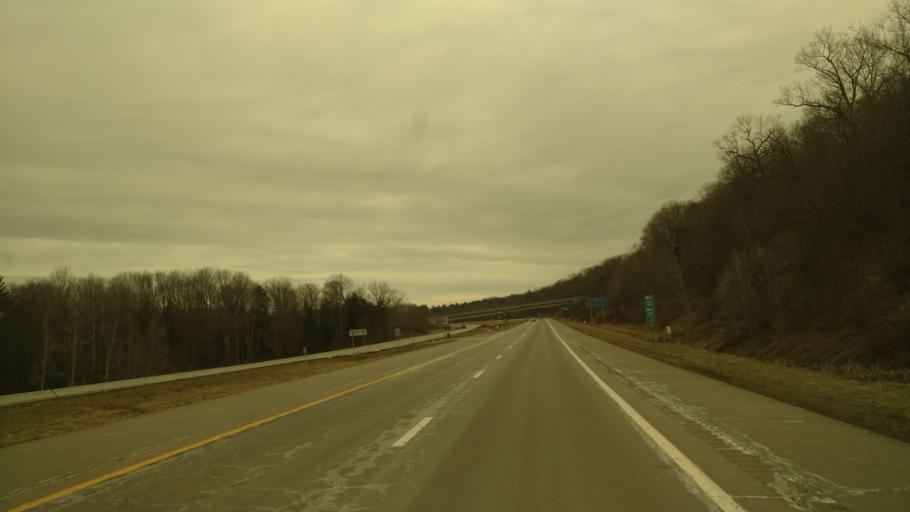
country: US
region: New York
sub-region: Chautauqua County
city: Falconer
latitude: 42.1246
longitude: -79.2194
